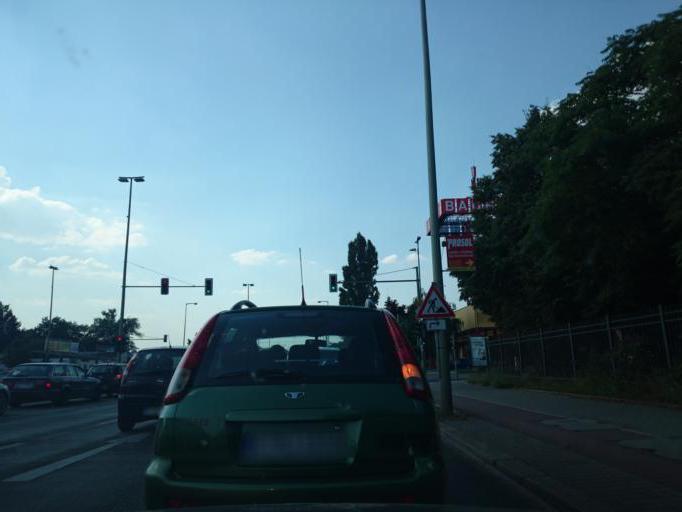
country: DE
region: Berlin
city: Niederschoneweide
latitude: 52.4604
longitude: 13.5044
